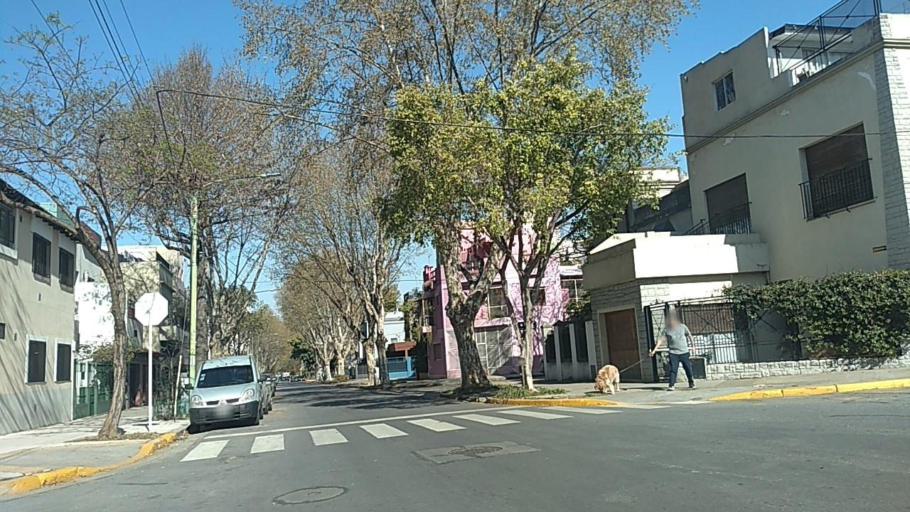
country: AR
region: Buenos Aires F.D.
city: Villa Santa Rita
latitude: -34.6096
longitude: -58.4864
